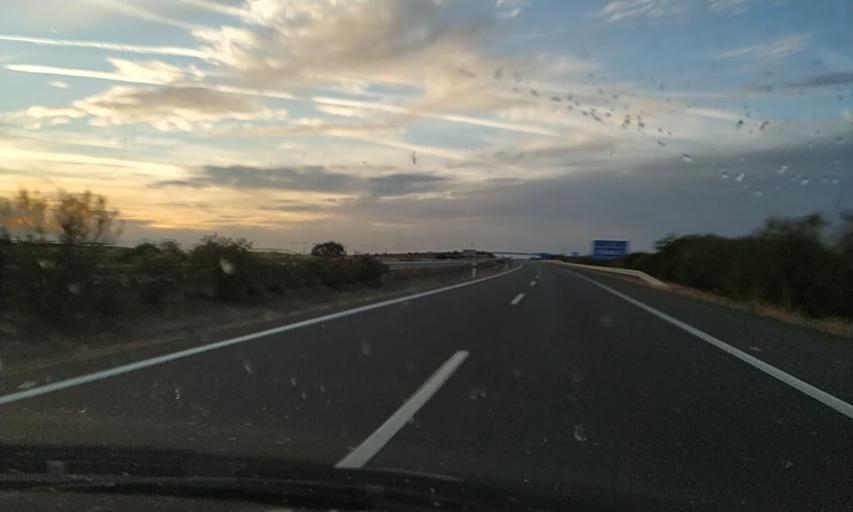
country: ES
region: Extremadura
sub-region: Provincia de Caceres
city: Aldea del Cano
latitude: 39.2783
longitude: -6.3247
